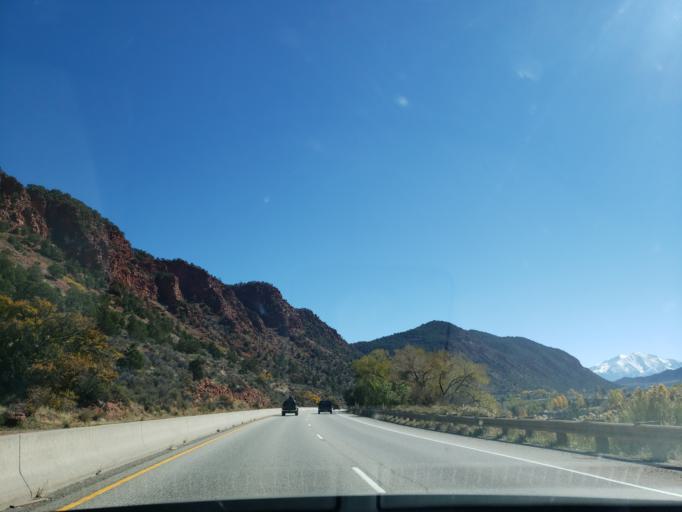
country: US
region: Colorado
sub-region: Garfield County
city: Glenwood Springs
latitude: 39.5145
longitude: -107.3115
